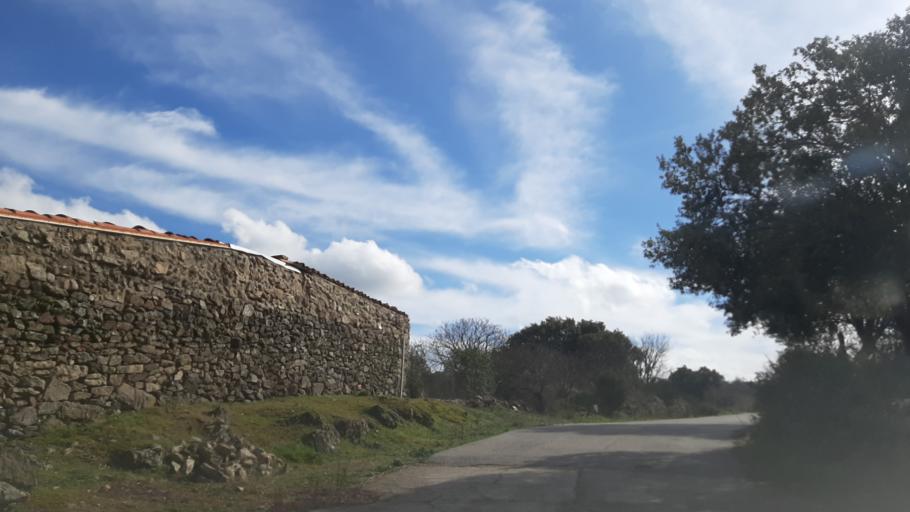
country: ES
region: Castille and Leon
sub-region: Provincia de Salamanca
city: Villarino de los Aires
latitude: 41.2591
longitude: -6.5264
